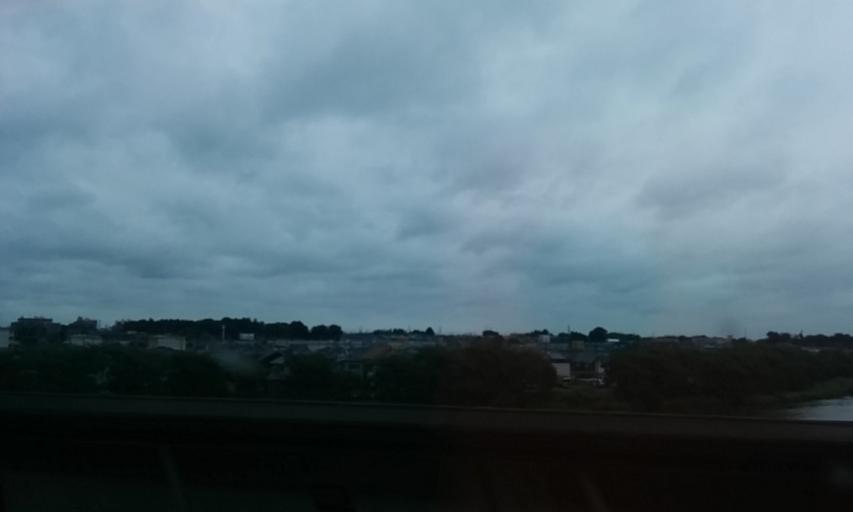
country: JP
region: Saitama
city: Shiraoka
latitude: 36.0126
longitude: 139.6488
